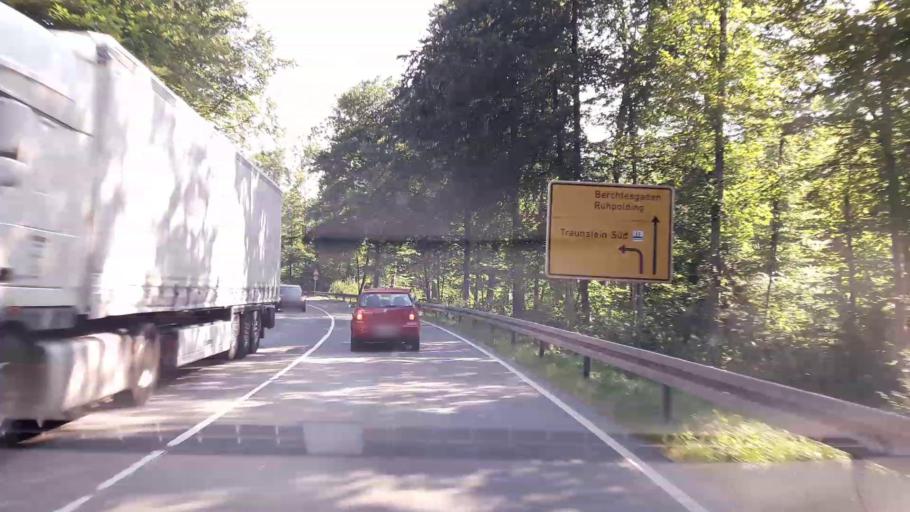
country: DE
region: Bavaria
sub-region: Upper Bavaria
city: Traunstein
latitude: 47.8595
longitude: 12.6378
